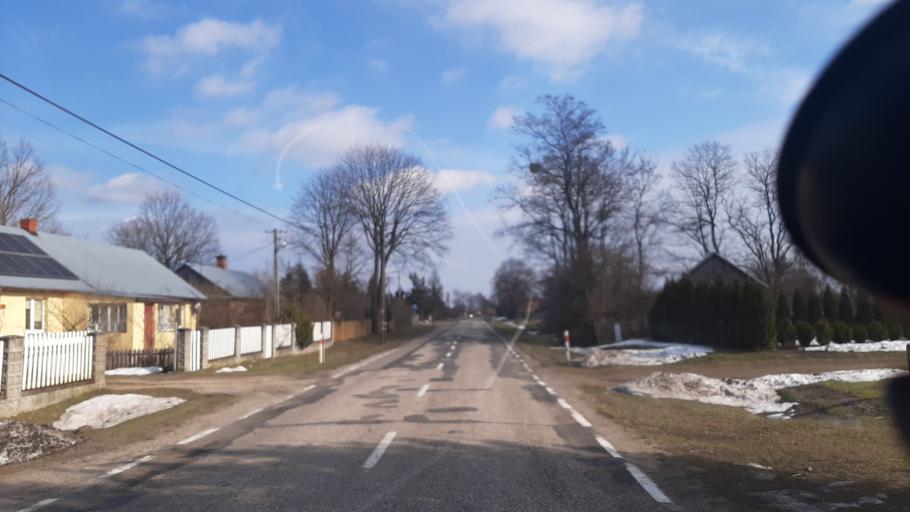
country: PL
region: Lublin Voivodeship
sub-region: Powiat wlodawski
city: Urszulin
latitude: 51.4934
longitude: 23.2305
